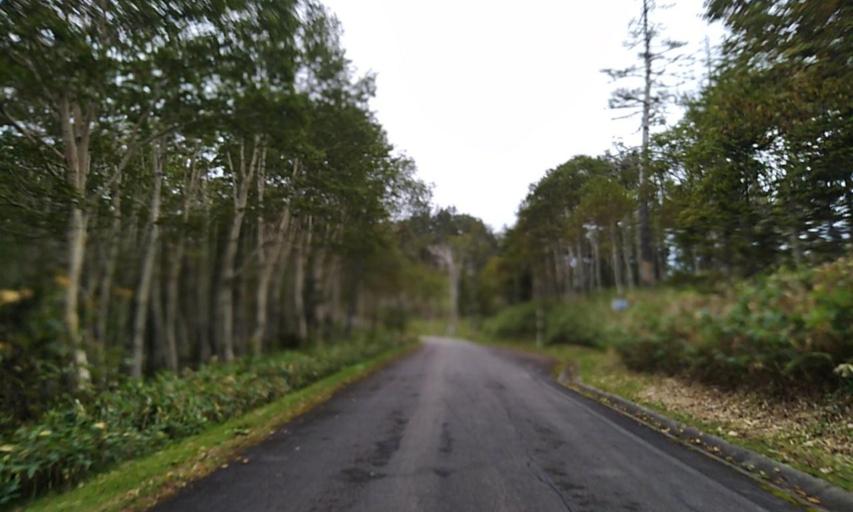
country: JP
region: Hokkaido
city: Bihoro
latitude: 43.5747
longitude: 144.2263
